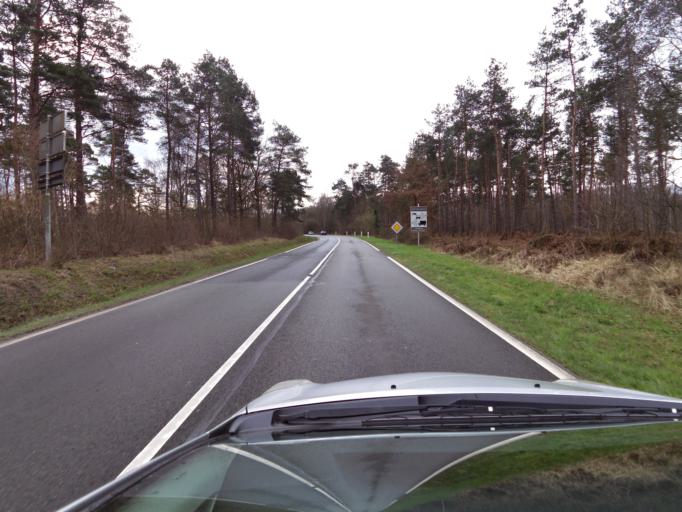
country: FR
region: Picardie
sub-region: Departement de l'Oise
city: Ver-sur-Launette
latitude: 49.1573
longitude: 2.6639
